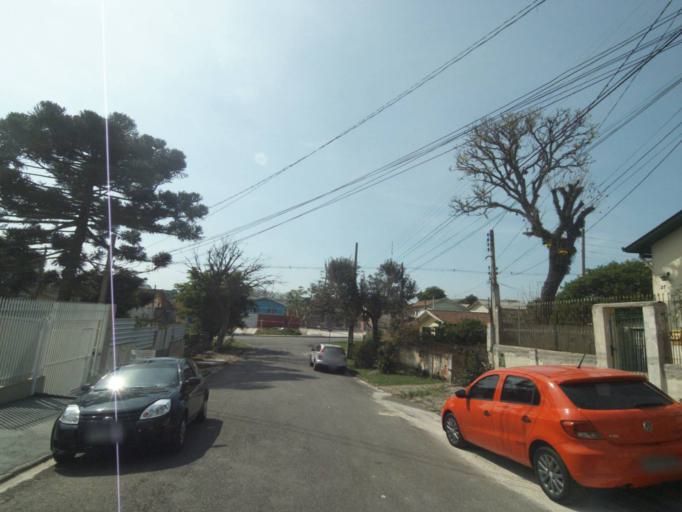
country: BR
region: Parana
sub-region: Curitiba
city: Curitiba
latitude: -25.4617
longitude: -49.3142
